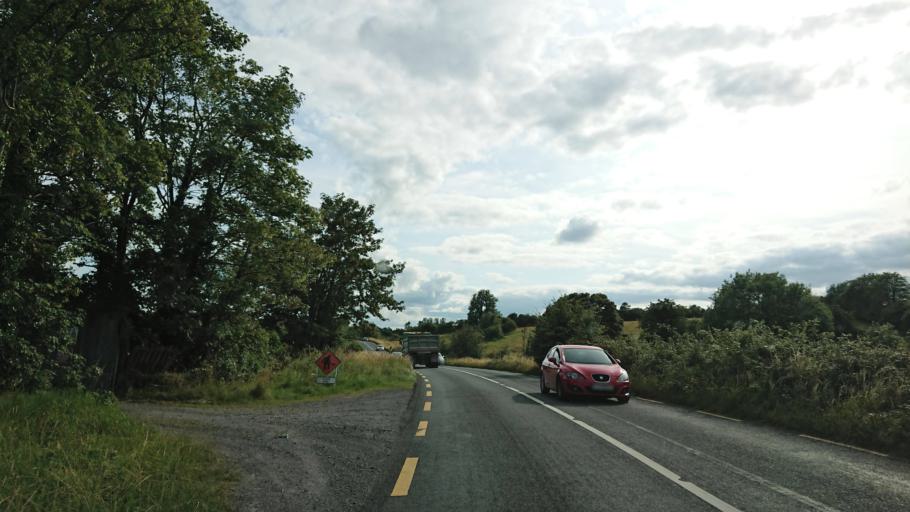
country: IE
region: Connaught
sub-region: County Leitrim
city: Carrick-on-Shannon
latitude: 53.9626
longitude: -8.0757
